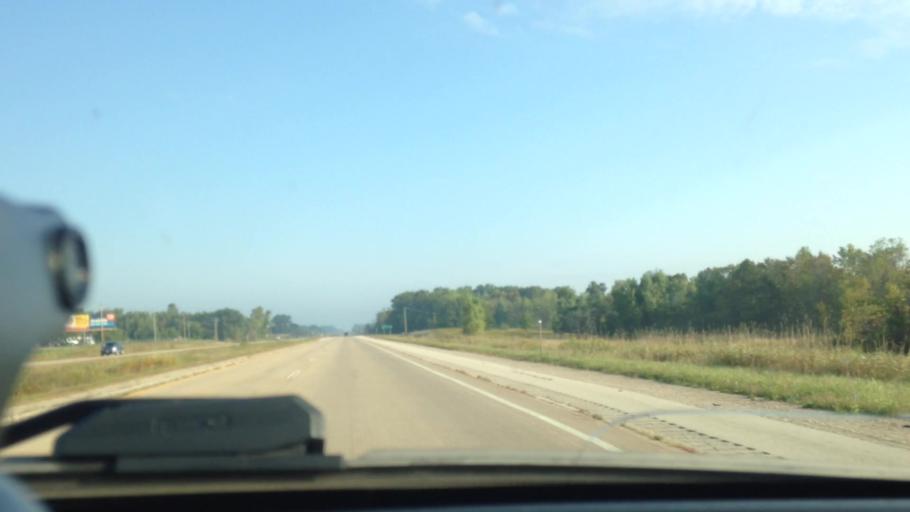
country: US
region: Wisconsin
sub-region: Oconto County
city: Oconto Falls
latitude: 44.9974
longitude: -88.0450
